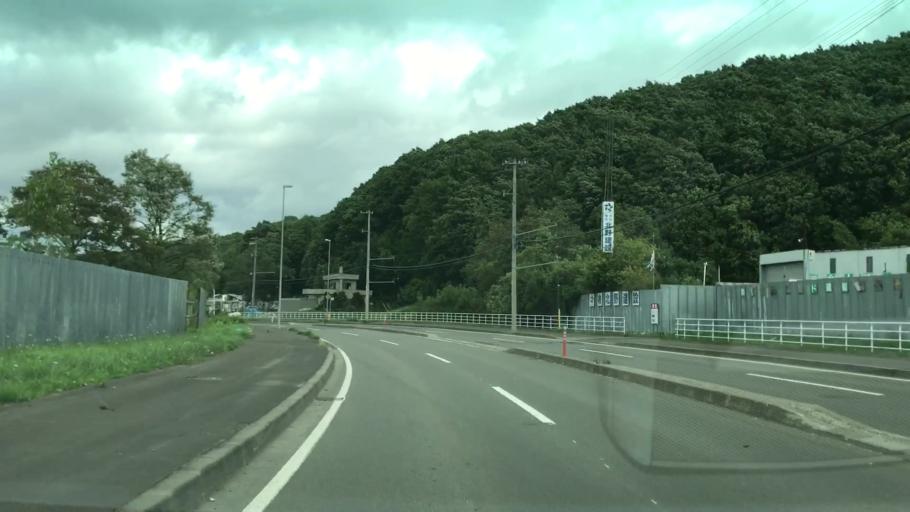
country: JP
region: Hokkaido
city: Kitahiroshima
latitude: 42.9668
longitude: 141.4551
